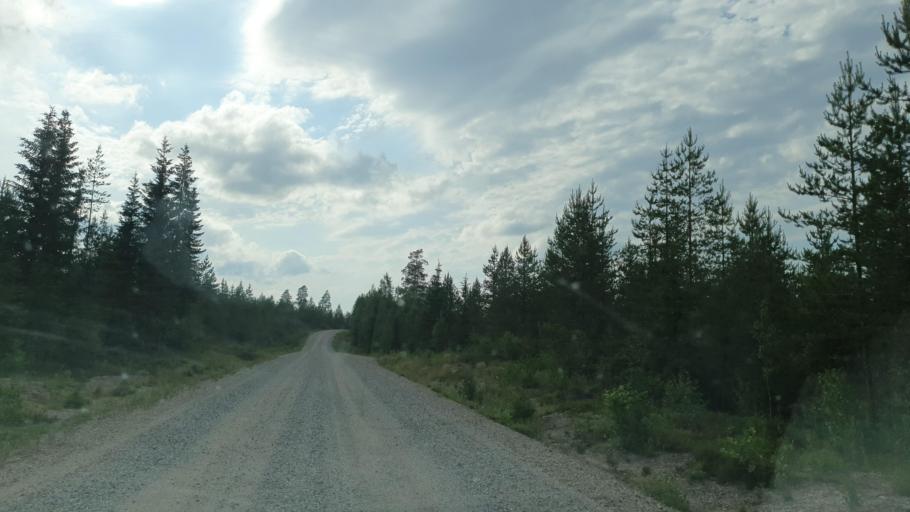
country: FI
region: Kainuu
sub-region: Kehys-Kainuu
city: Kuhmo
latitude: 64.0222
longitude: 29.8855
